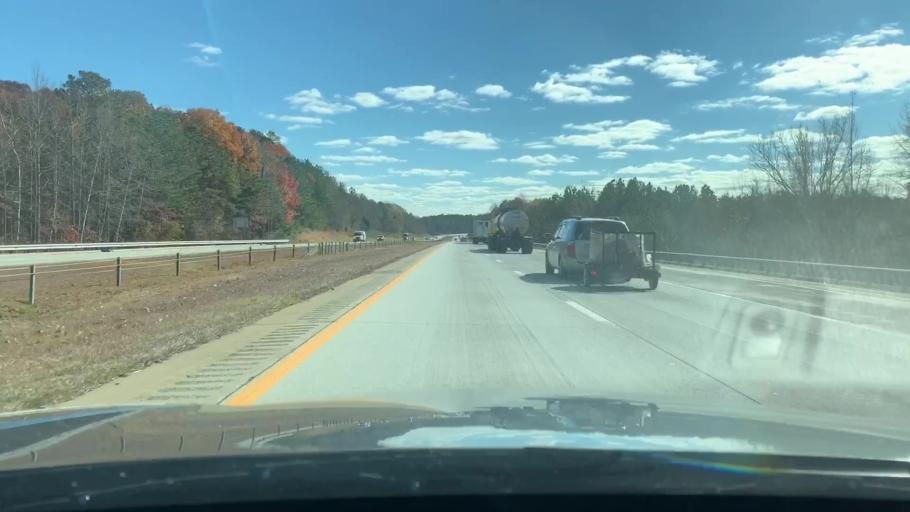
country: US
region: North Carolina
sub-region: Orange County
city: Hillsborough
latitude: 36.0047
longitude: -79.0813
